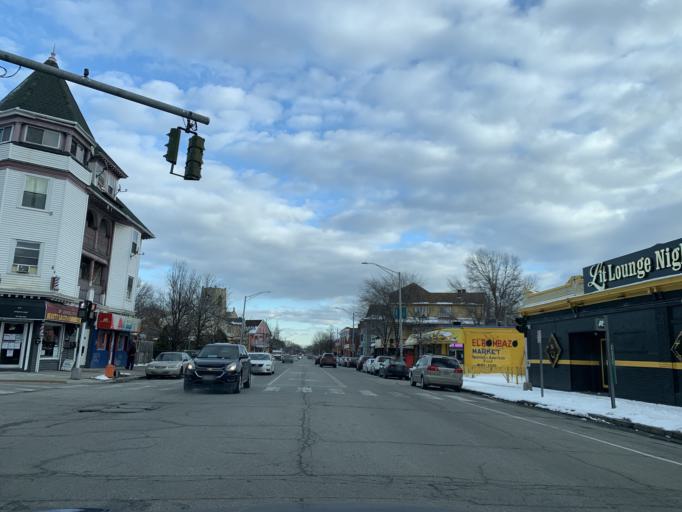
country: US
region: Rhode Island
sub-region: Providence County
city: Providence
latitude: 41.7983
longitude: -71.4148
